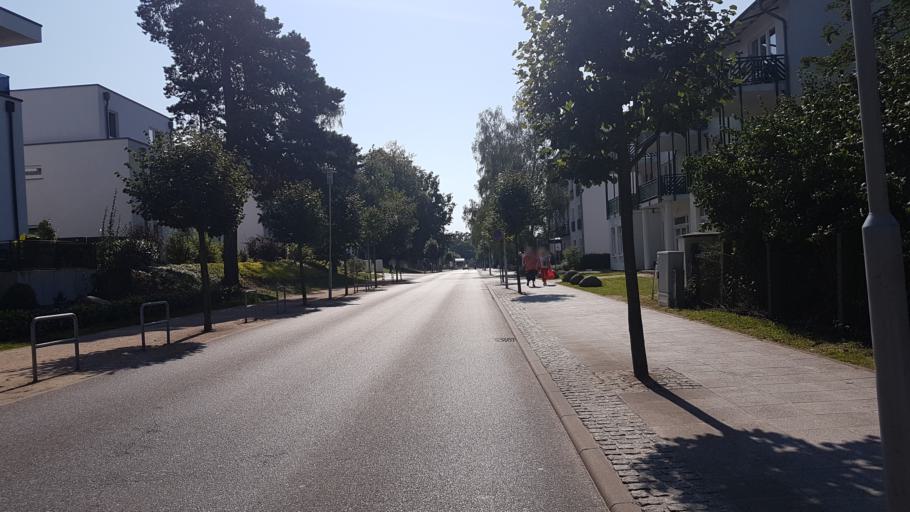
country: DE
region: Mecklenburg-Vorpommern
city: Ostseebad Sellin
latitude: 54.3745
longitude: 13.6996
